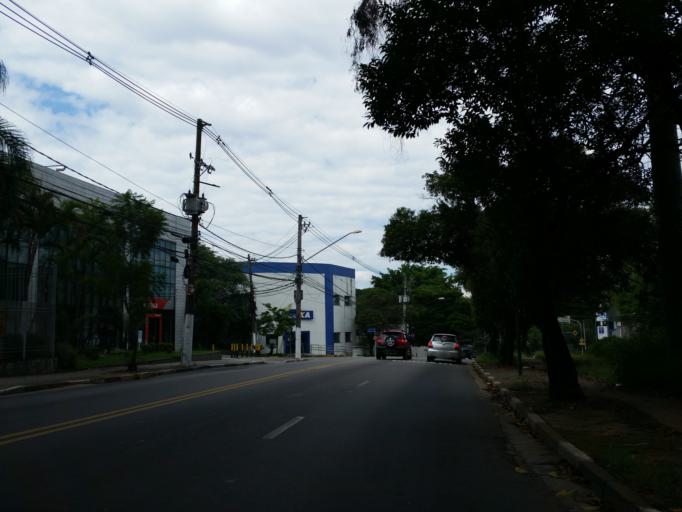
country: BR
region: Sao Paulo
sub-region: Diadema
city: Diadema
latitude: -23.6521
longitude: -46.6819
